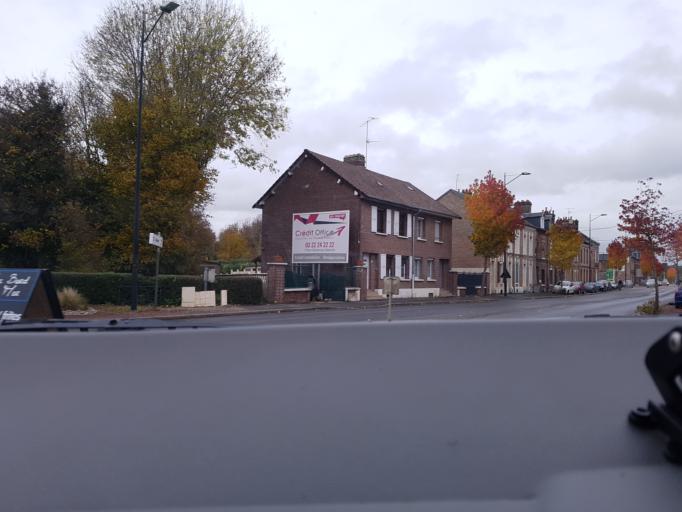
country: FR
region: Picardie
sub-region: Departement de la Somme
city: Abbeville
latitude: 50.1139
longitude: 1.8267
